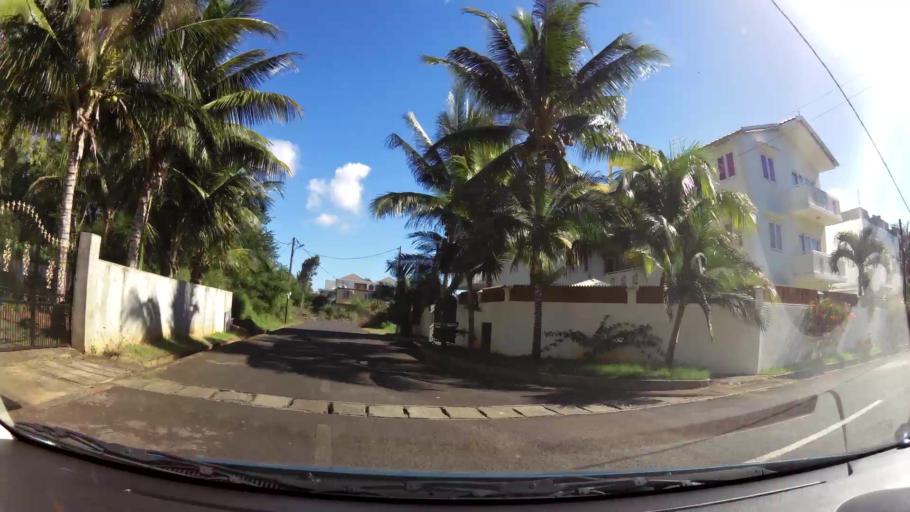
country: MU
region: Black River
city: Flic en Flac
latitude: -20.2853
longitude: 57.3698
